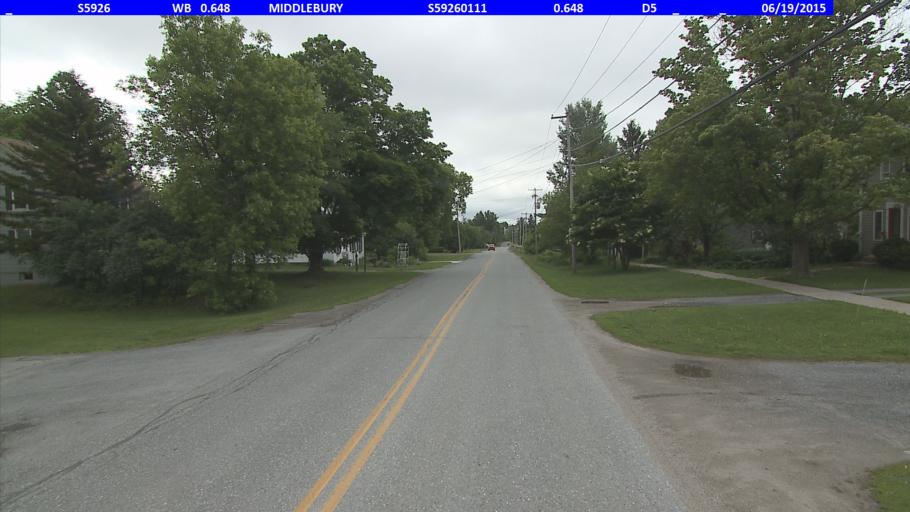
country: US
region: Vermont
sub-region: Addison County
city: Middlebury (village)
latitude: 44.0213
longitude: -73.1733
